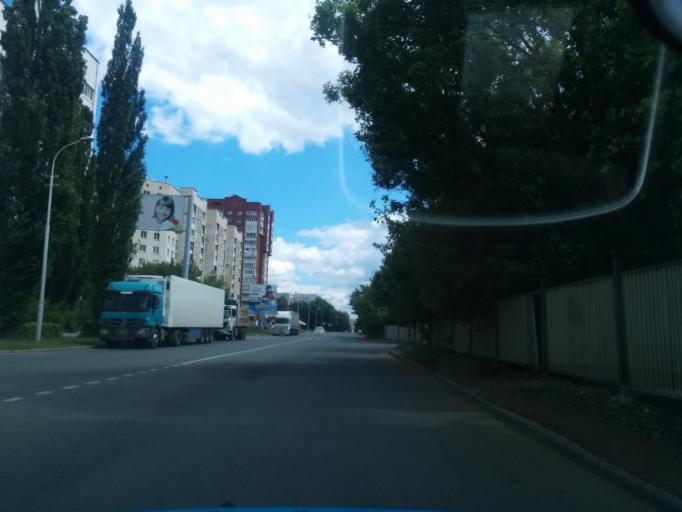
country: RU
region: Bashkortostan
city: Ufa
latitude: 54.7264
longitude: 55.9618
